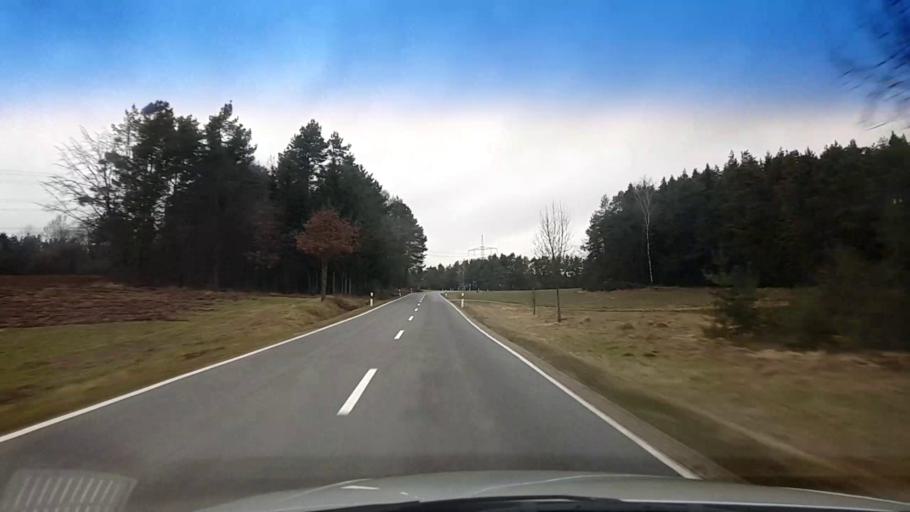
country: DE
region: Bavaria
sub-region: Upper Franconia
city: Wattendorf
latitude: 50.0177
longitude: 11.1280
